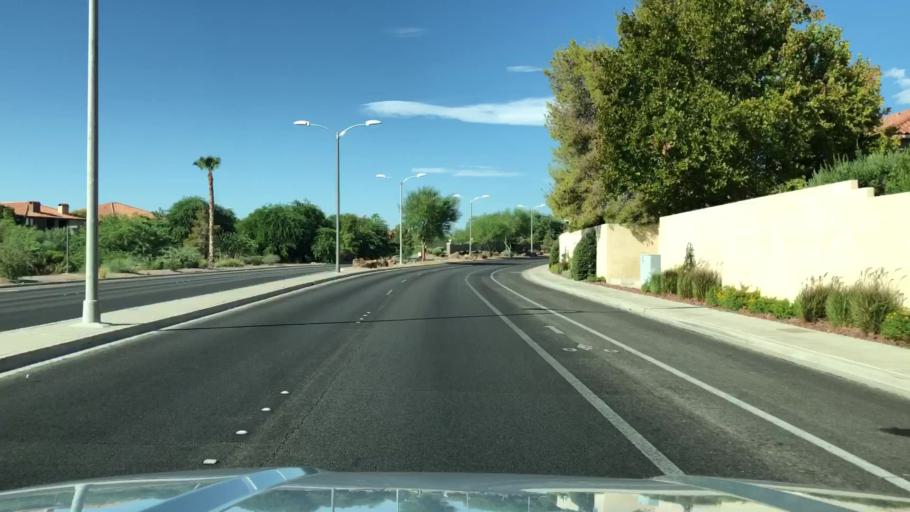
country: US
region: Nevada
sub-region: Clark County
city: Whitney
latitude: 36.0430
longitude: -115.0845
